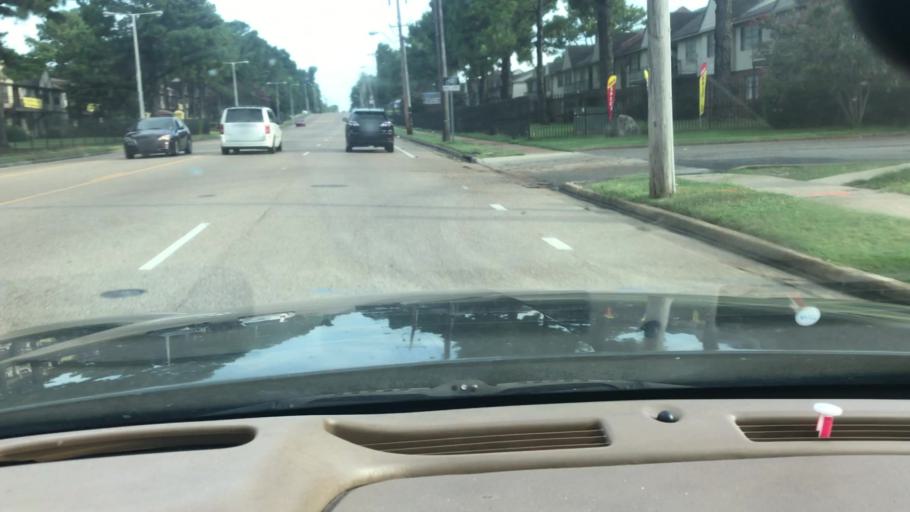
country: US
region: Tennessee
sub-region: Shelby County
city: New South Memphis
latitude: 35.0523
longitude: -90.0075
